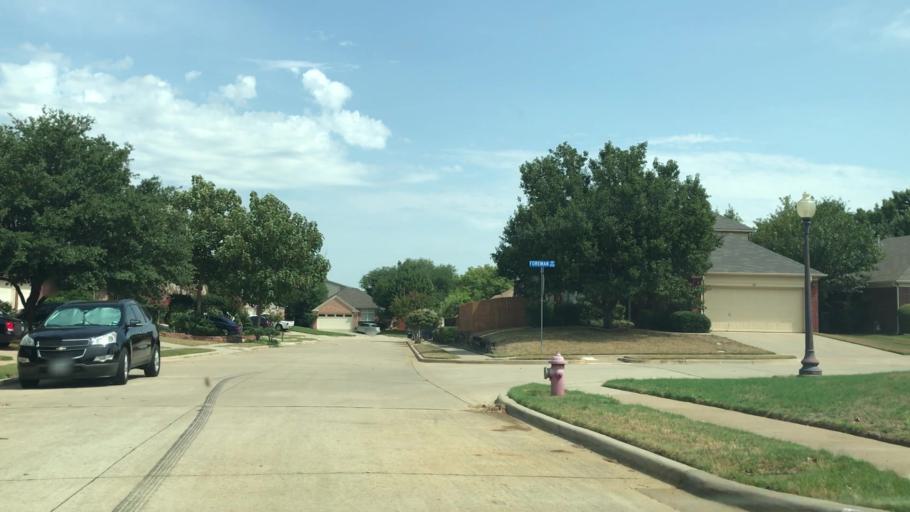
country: US
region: Texas
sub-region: Tarrant County
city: Euless
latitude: 32.8541
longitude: -97.0798
